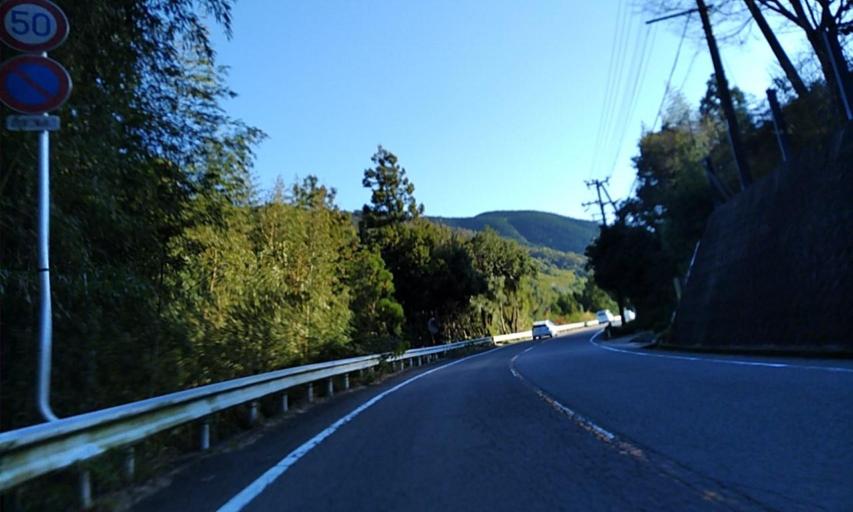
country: JP
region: Wakayama
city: Iwade
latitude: 34.1569
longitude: 135.3229
